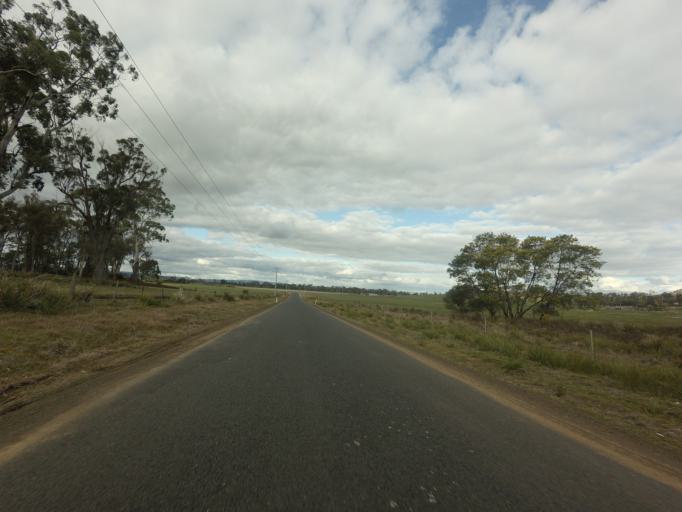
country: AU
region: Tasmania
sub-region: Northern Midlands
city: Evandale
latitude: -41.8663
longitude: 147.2832
